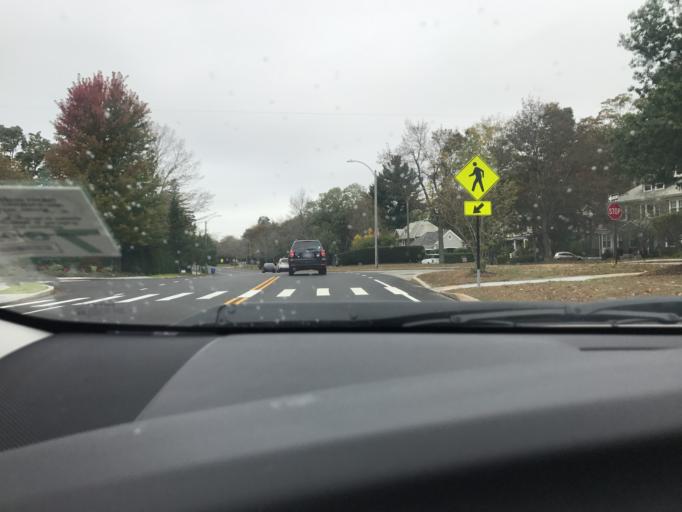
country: US
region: Massachusetts
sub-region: Middlesex County
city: Newton
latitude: 42.3379
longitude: -71.1983
